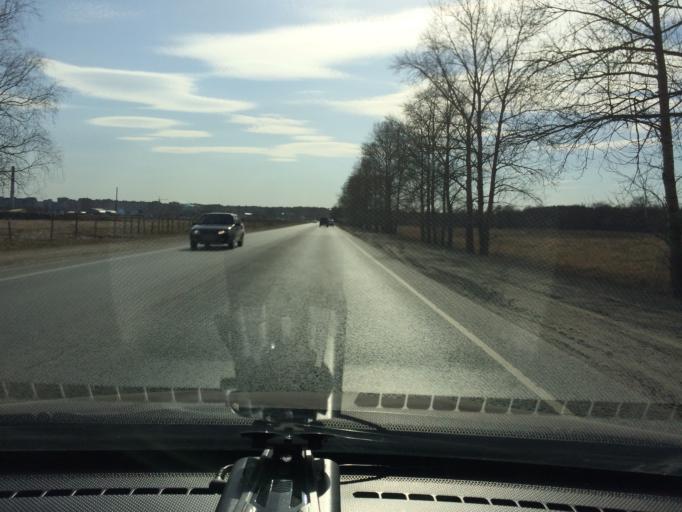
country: RU
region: Mariy-El
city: Yoshkar-Ola
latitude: 56.6502
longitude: 47.9458
